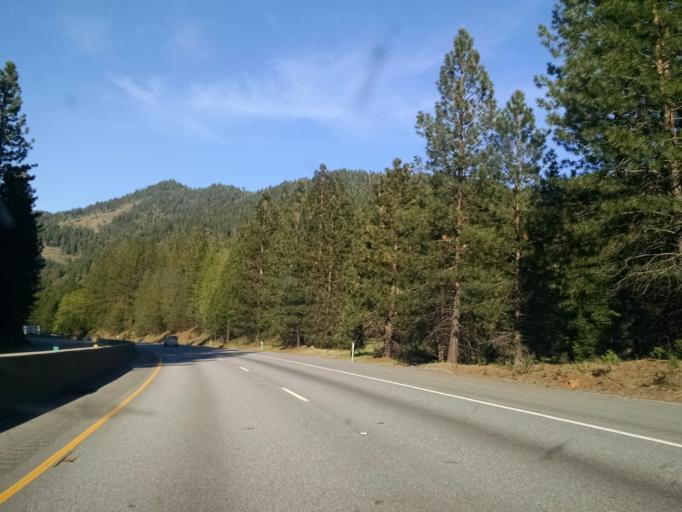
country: US
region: California
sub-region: Siskiyou County
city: Dunsmuir
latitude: 41.0651
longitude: -122.3649
